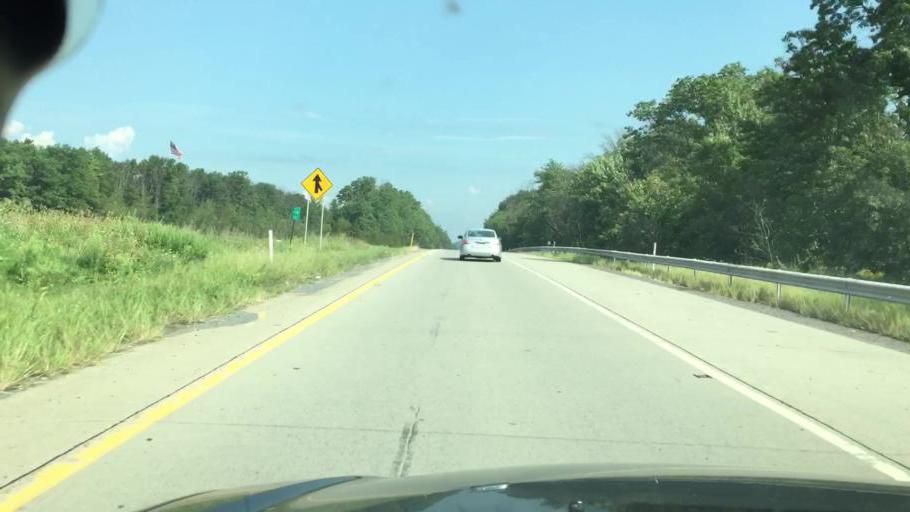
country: US
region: Pennsylvania
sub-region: Luzerne County
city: Freeland
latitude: 41.0817
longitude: -75.9621
